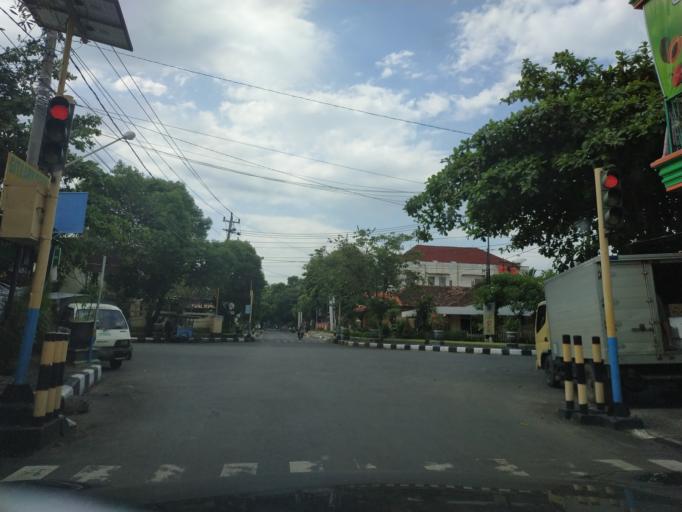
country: ID
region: Central Java
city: Pati
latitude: -6.7548
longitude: 111.0327
